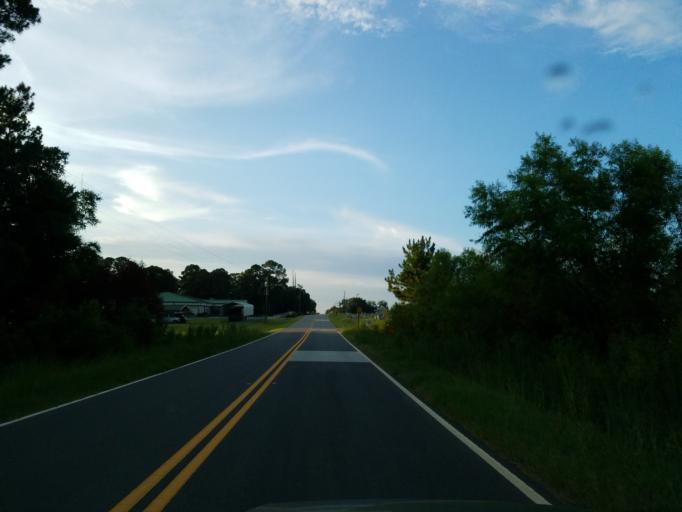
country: US
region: Georgia
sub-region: Turner County
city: Ashburn
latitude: 31.6563
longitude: -83.5662
